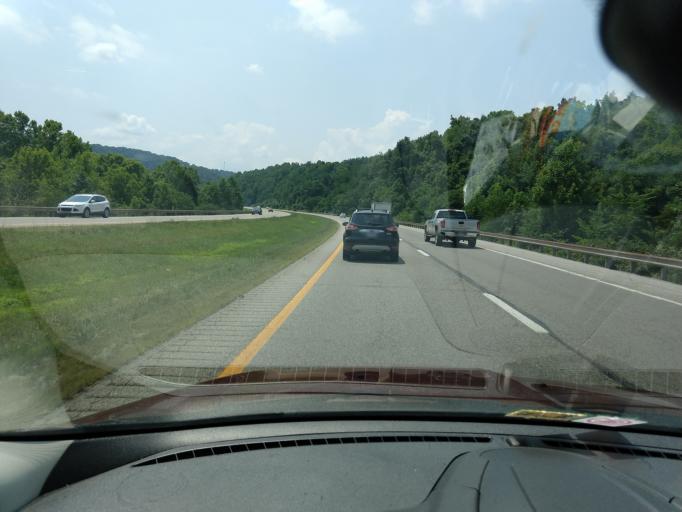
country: US
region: West Virginia
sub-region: Kanawha County
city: Sissonville
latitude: 38.4859
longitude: -81.6458
